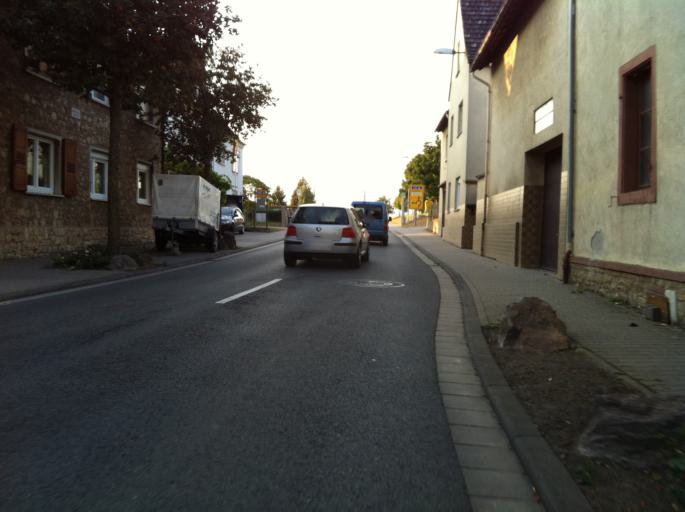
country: DE
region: Rheinland-Pfalz
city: Bubenheim
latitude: 49.9451
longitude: 8.0770
